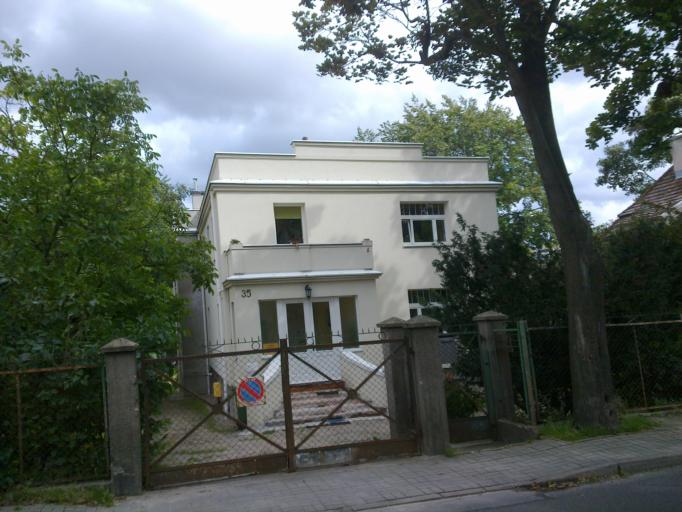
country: PL
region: Pomeranian Voivodeship
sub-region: Gdynia
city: Gdynia
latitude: 54.5117
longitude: 18.5492
